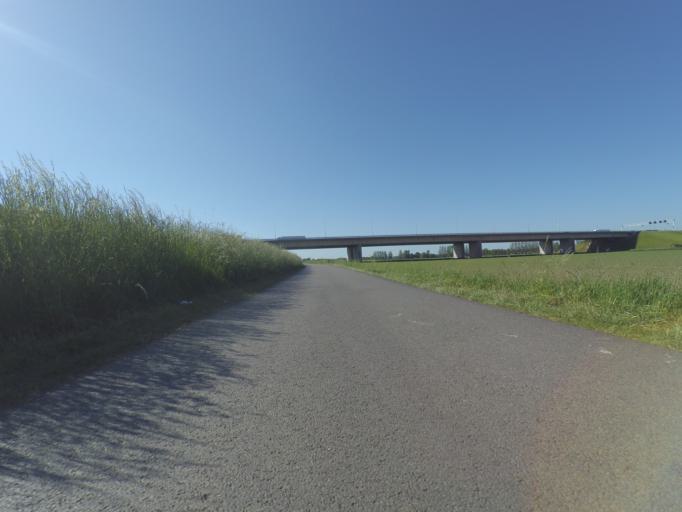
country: NL
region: Gelderland
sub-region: Gemeente Voorst
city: Wilp
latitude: 52.2310
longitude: 6.1597
